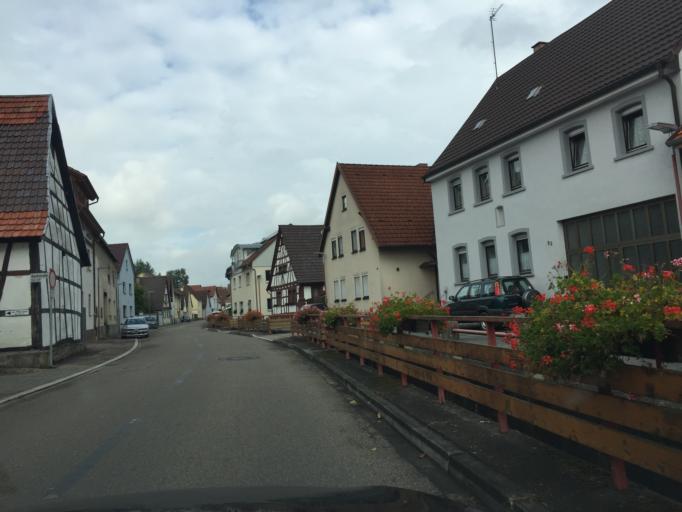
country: DE
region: Baden-Wuerttemberg
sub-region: Karlsruhe Region
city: Ubstadt-Weiher
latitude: 49.1509
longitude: 8.6921
